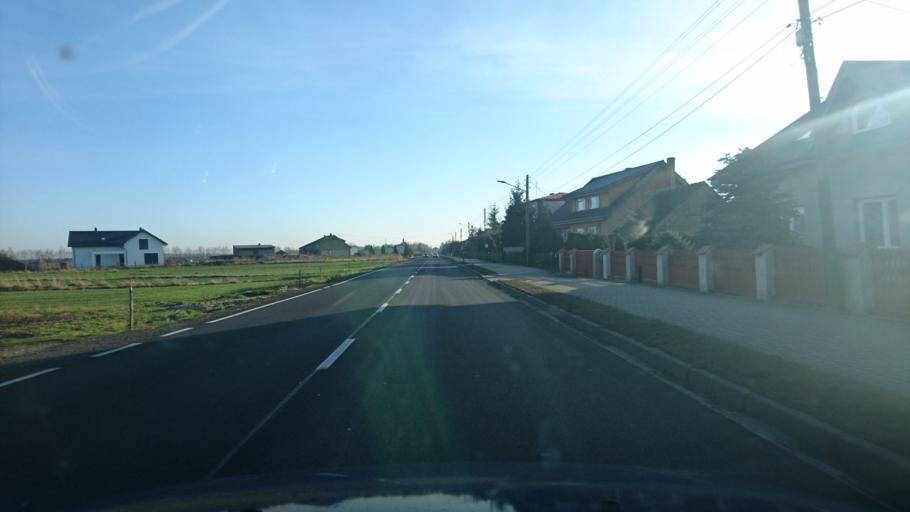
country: PL
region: Silesian Voivodeship
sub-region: Powiat klobucki
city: Starokrzepice
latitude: 51.0003
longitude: 18.6663
